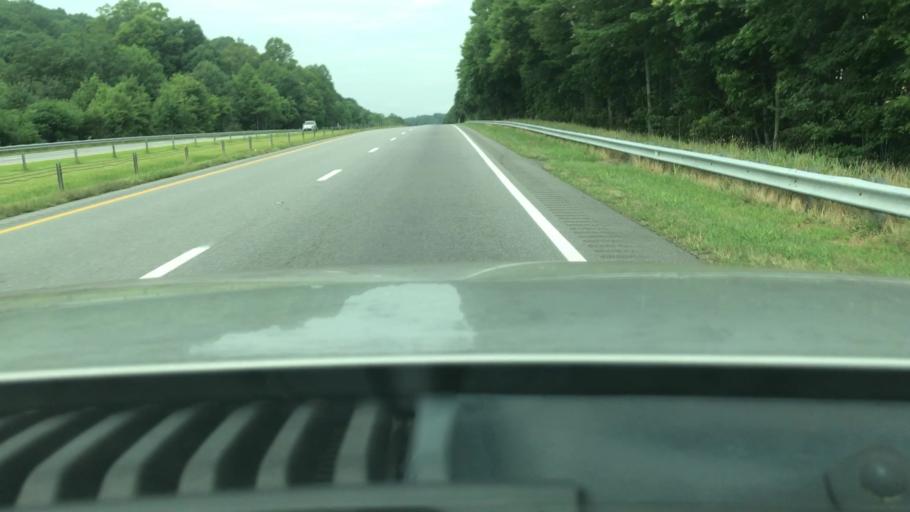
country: US
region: North Carolina
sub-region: Wilkes County
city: North Wilkesboro
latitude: 36.1474
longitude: -81.0419
